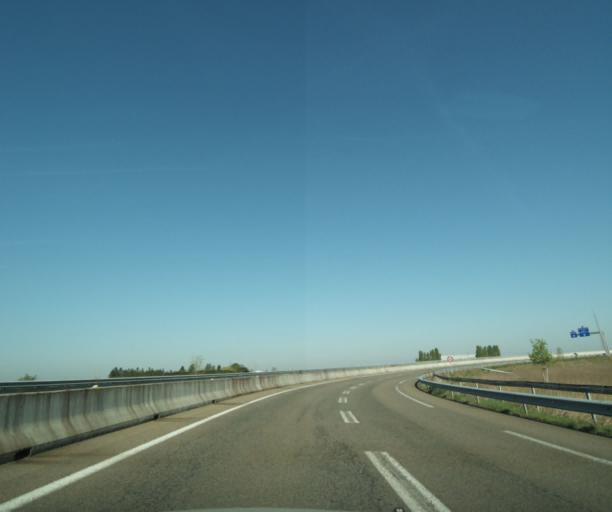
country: FR
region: Centre
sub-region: Departement du Loiret
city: Pannes
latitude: 48.0613
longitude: 2.6637
